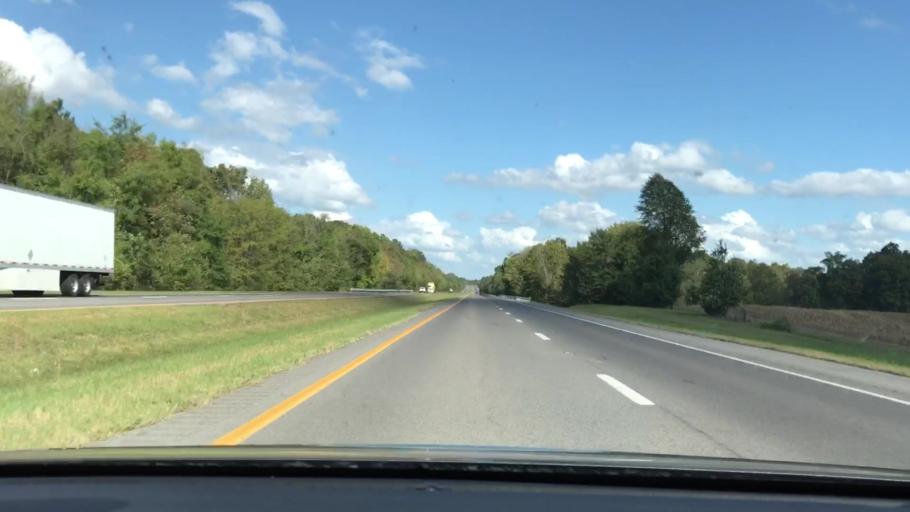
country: US
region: Kentucky
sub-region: Marshall County
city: Benton
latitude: 36.8288
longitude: -88.4534
